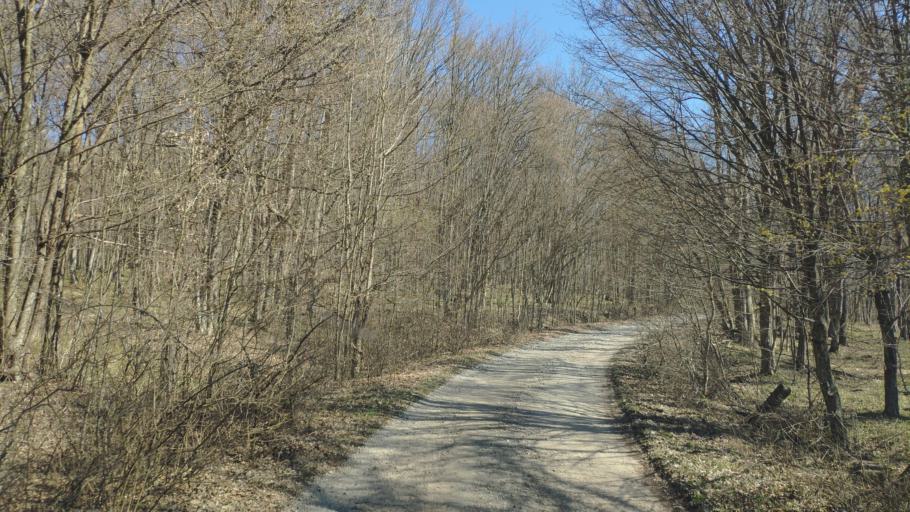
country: SK
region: Kosicky
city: Roznava
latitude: 48.5863
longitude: 20.4067
